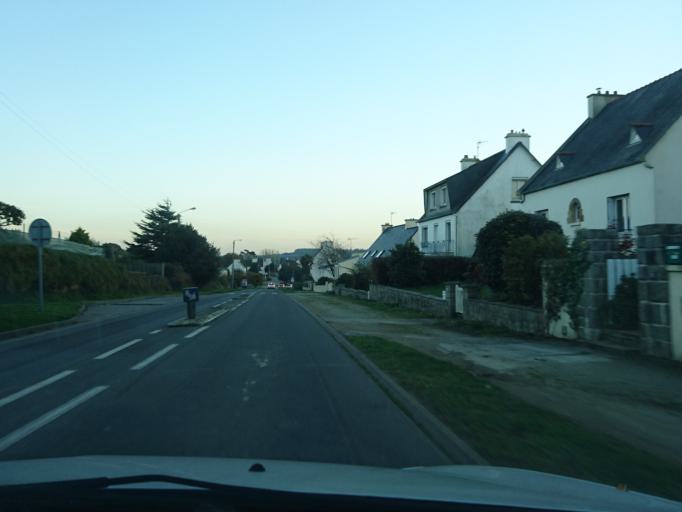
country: FR
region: Brittany
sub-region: Departement du Finistere
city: Saint-Renan
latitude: 48.4397
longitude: -4.6204
